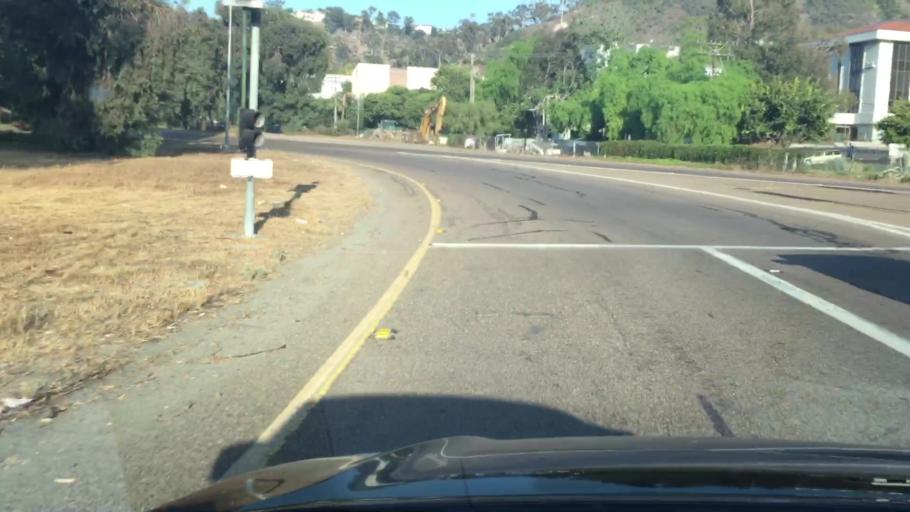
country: US
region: California
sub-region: San Diego County
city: San Diego
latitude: 32.7698
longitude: -117.1373
